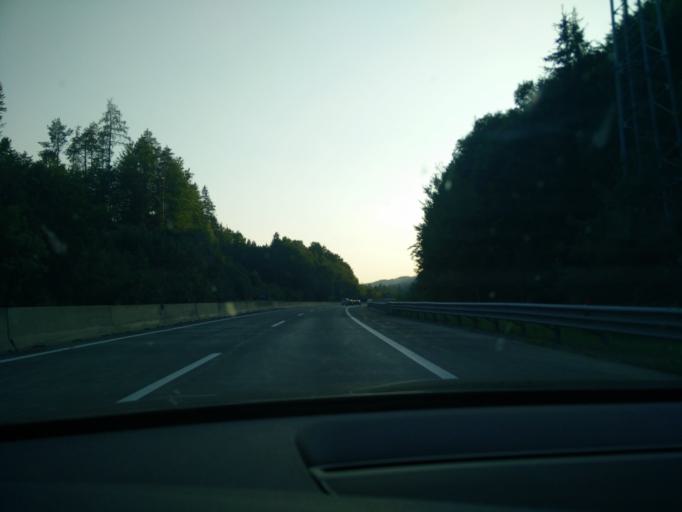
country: AT
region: Carinthia
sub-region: Politischer Bezirk Klagenfurt Land
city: Maria Worth
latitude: 46.6390
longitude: 14.1256
